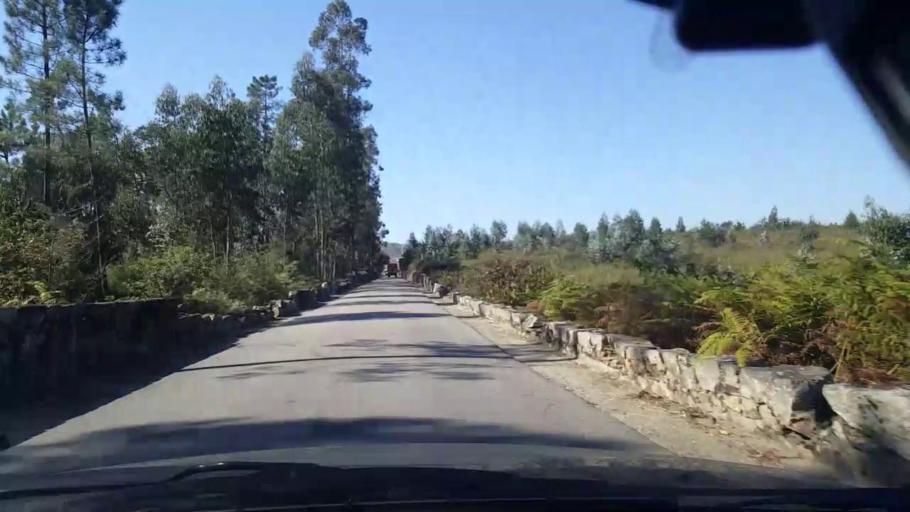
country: PT
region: Braga
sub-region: Vila Nova de Famalicao
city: Ribeirao
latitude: 41.3571
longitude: -8.6404
